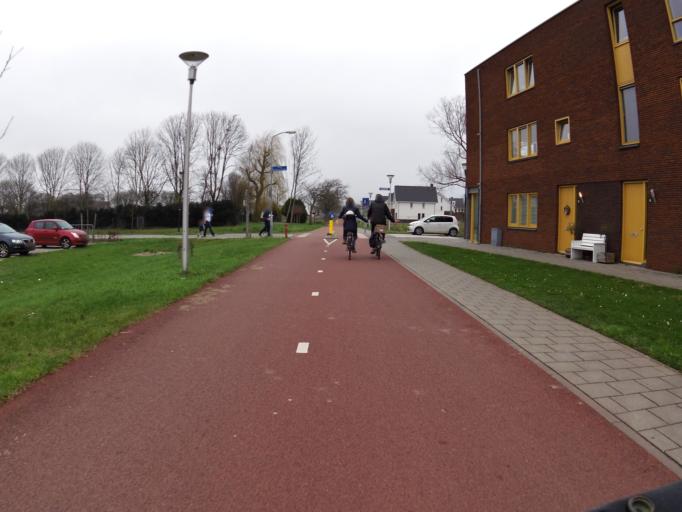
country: NL
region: Gelderland
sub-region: Gemeente Nijmegen
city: Nijmegen
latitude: 51.8700
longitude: 5.8653
